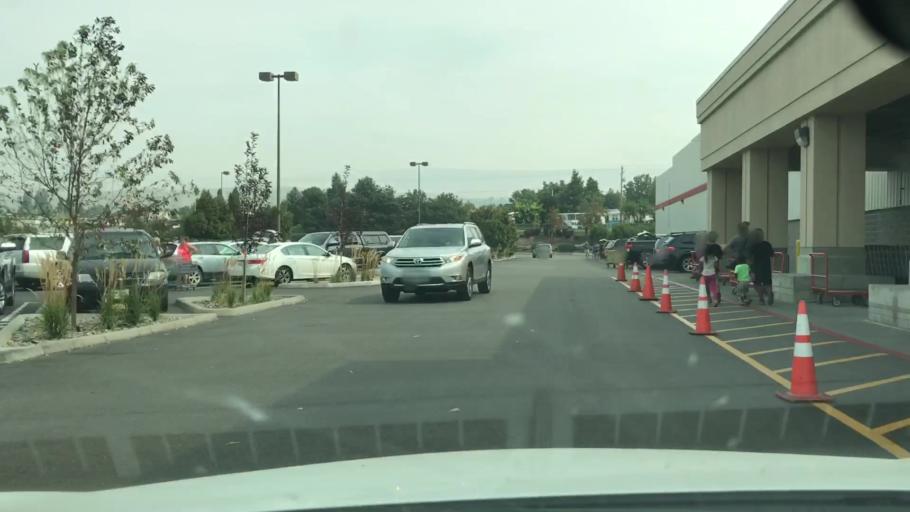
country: US
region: Washington
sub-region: Chelan County
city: South Wenatchee
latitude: 47.4015
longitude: -120.2809
